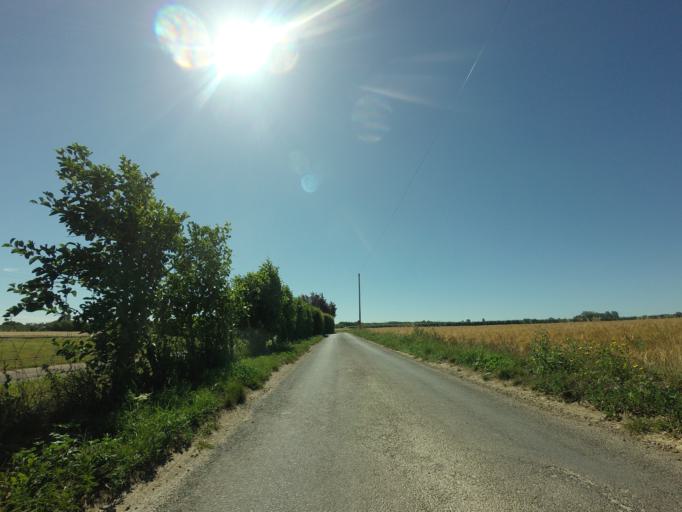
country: GB
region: England
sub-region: Kent
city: Ash
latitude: 51.2928
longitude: 1.2453
